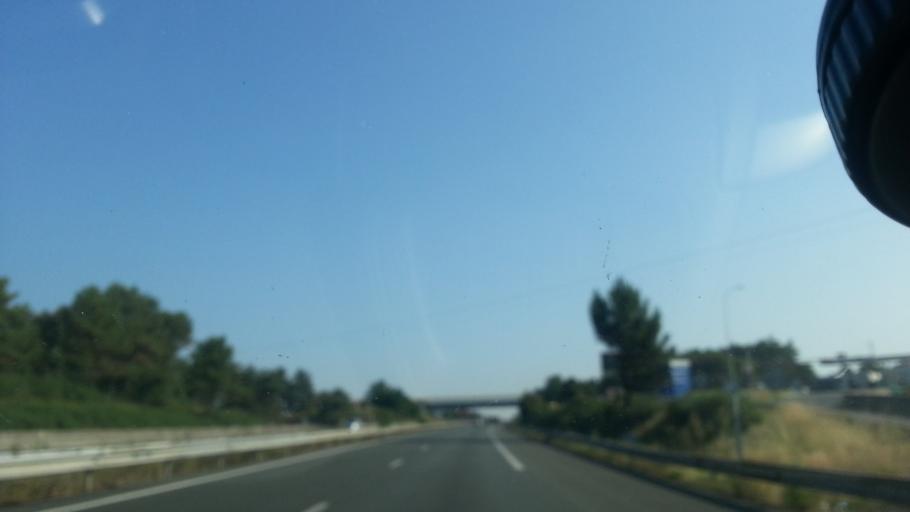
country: FR
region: Poitou-Charentes
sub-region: Departement de la Vienne
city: Antran
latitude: 46.9040
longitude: 0.5219
